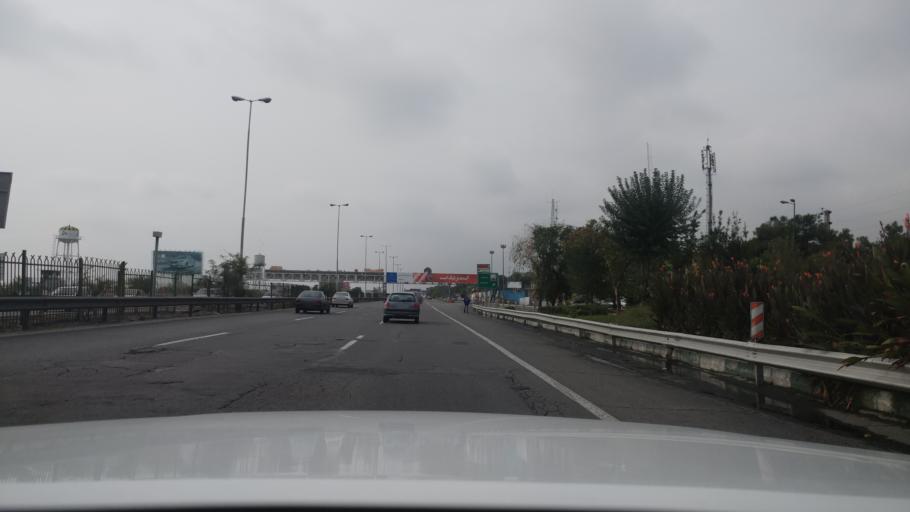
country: IR
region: Tehran
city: Shahr-e Qods
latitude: 35.7161
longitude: 51.2409
